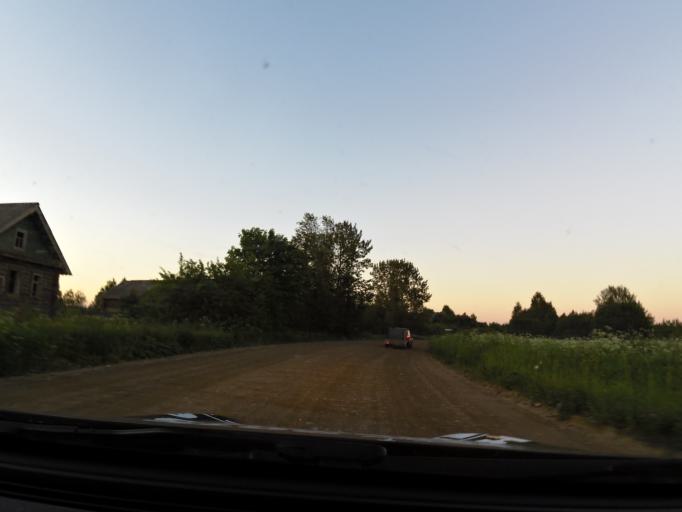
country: RU
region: Leningrad
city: Voznesen'ye
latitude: 60.8384
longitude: 35.7733
